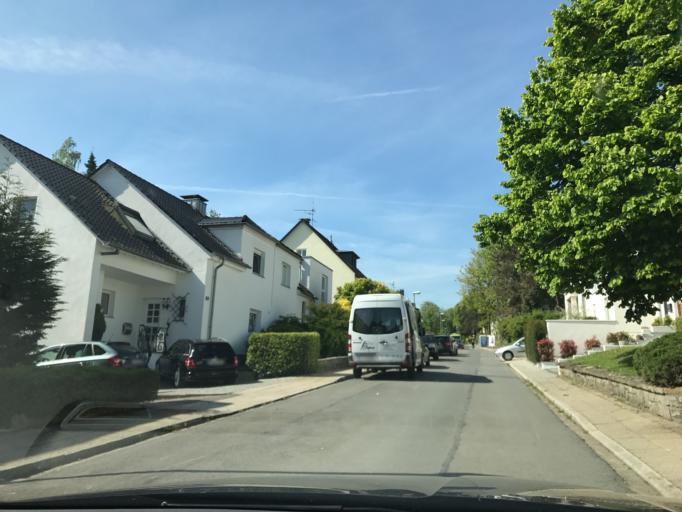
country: DE
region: North Rhine-Westphalia
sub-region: Regierungsbezirk Dusseldorf
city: Essen
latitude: 51.4183
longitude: 7.0475
